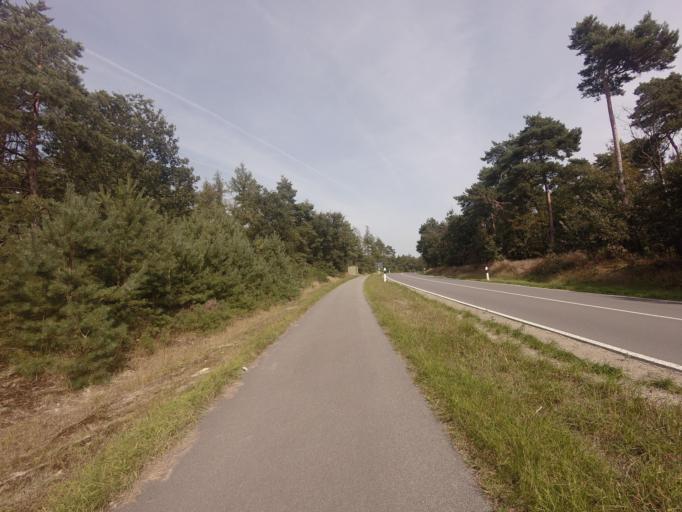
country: DE
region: Lower Saxony
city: Wielen
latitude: 52.5287
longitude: 6.7289
